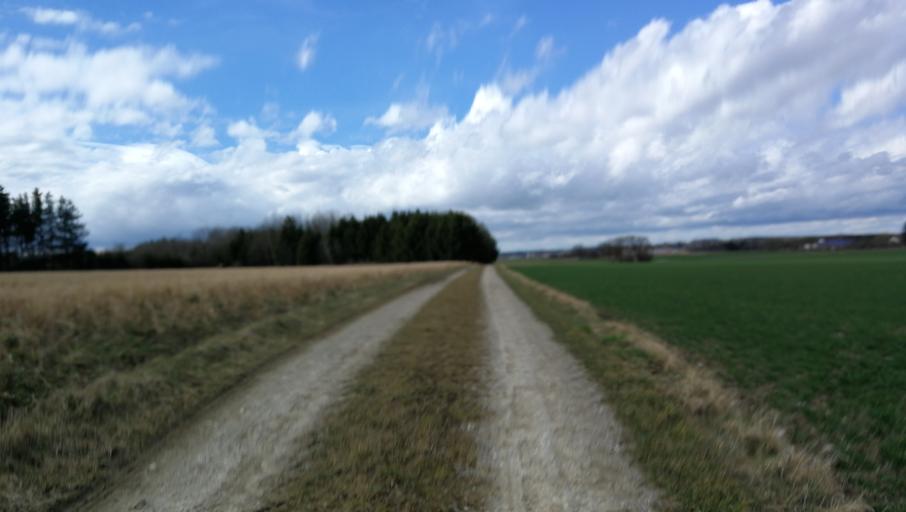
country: DE
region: Bavaria
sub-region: Upper Bavaria
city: Fuerstenfeldbruck
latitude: 48.2007
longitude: 11.2078
